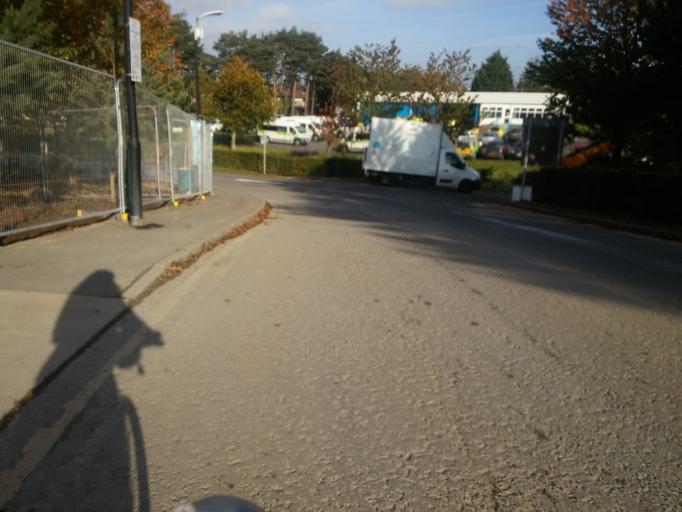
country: GB
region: Northern Ireland
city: Londonderry County Borough
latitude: 54.9871
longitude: -7.2897
